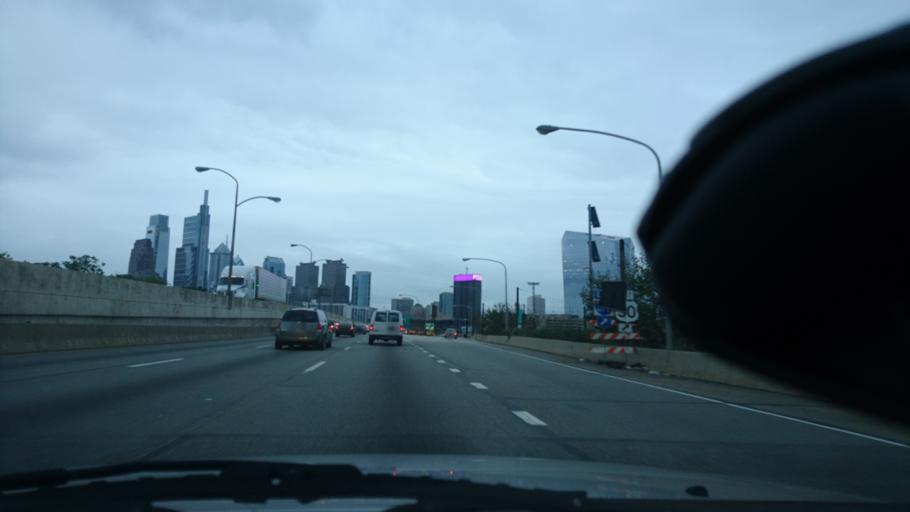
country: US
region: Pennsylvania
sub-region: Philadelphia County
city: Philadelphia
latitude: 39.9635
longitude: -75.1842
